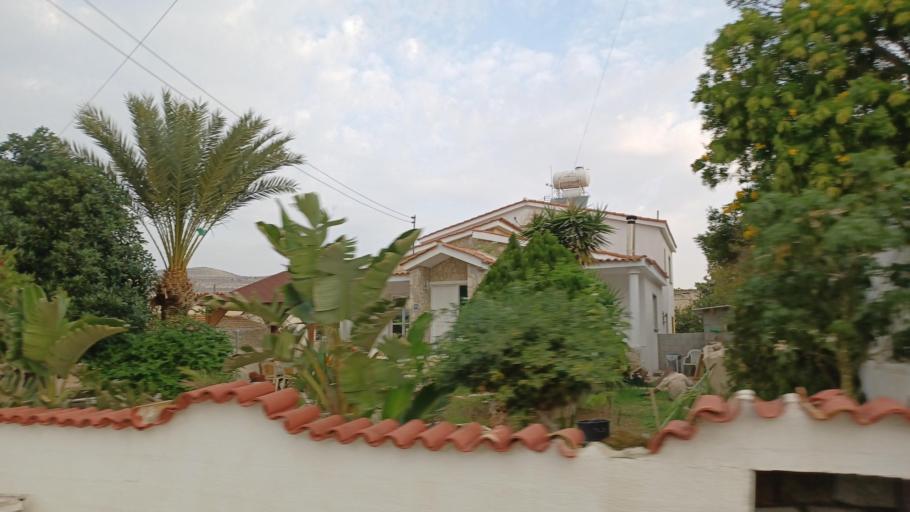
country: CY
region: Larnaka
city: Troulloi
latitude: 35.0103
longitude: 33.5715
